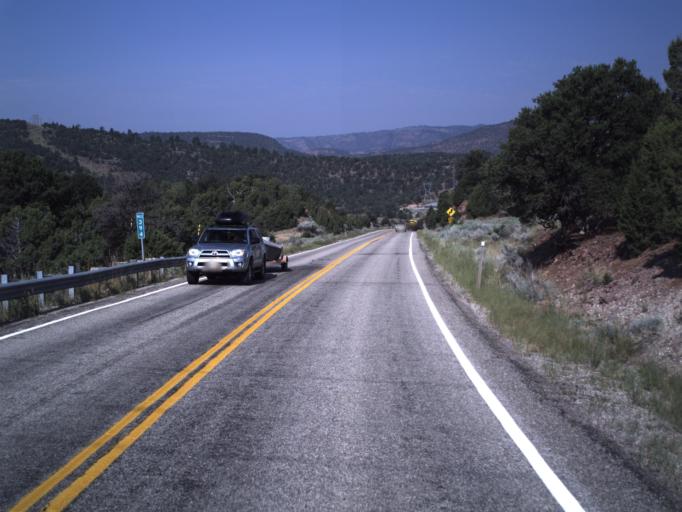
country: US
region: Utah
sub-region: Daggett County
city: Manila
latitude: 40.9110
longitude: -109.4144
